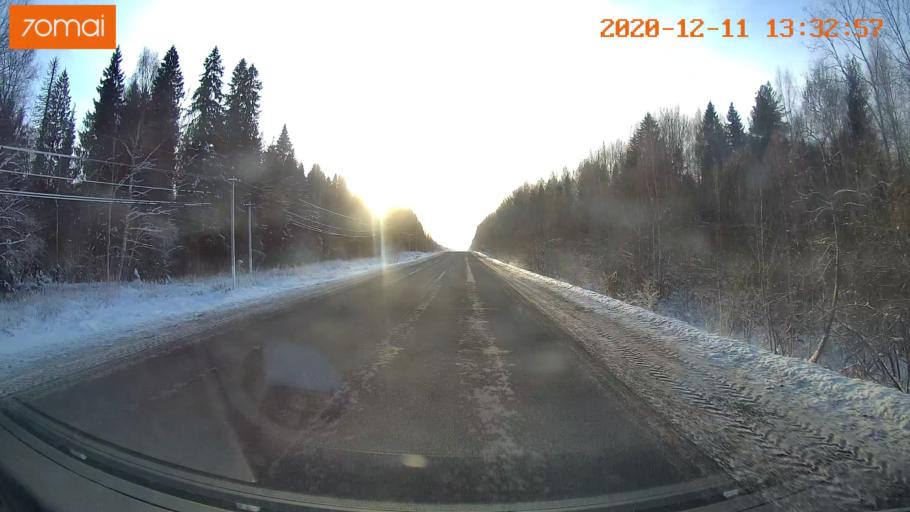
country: RU
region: Kostroma
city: Oktyabr'skiy
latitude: 57.9590
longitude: 41.2696
